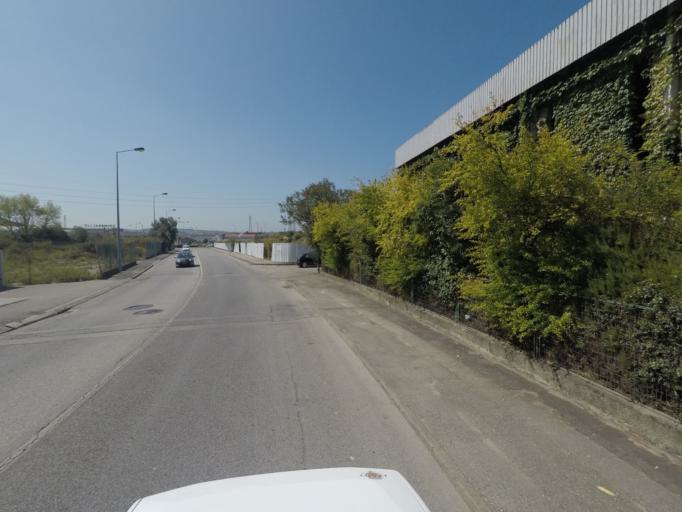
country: PT
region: Coimbra
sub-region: Coimbra
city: Coimbra
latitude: 40.2406
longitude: -8.4349
